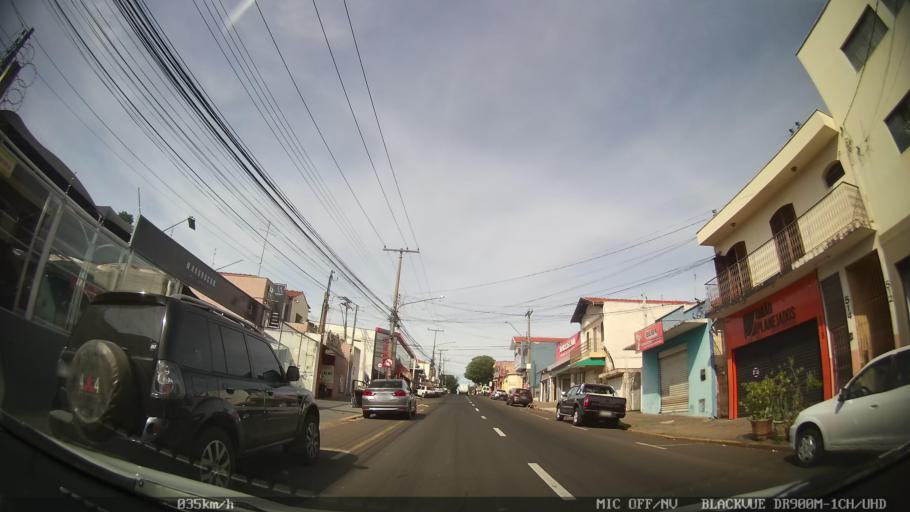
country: BR
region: Sao Paulo
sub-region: Piracicaba
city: Piracicaba
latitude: -22.7437
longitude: -47.6514
